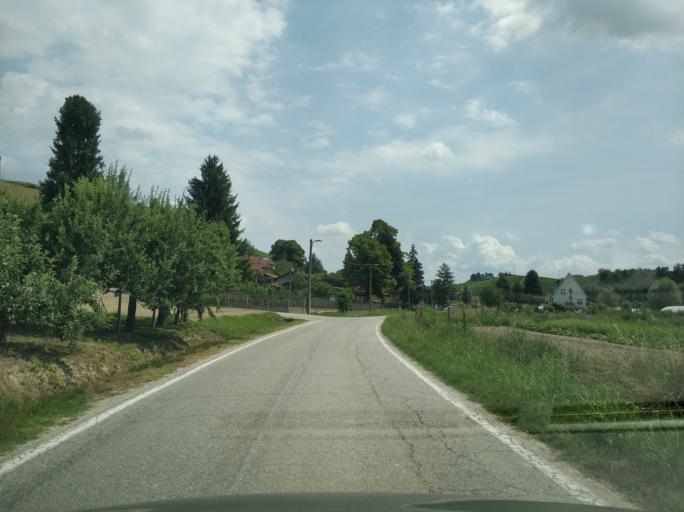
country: IT
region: Piedmont
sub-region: Provincia di Cuneo
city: Santo Stefano Roero
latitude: 44.7854
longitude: 7.9665
